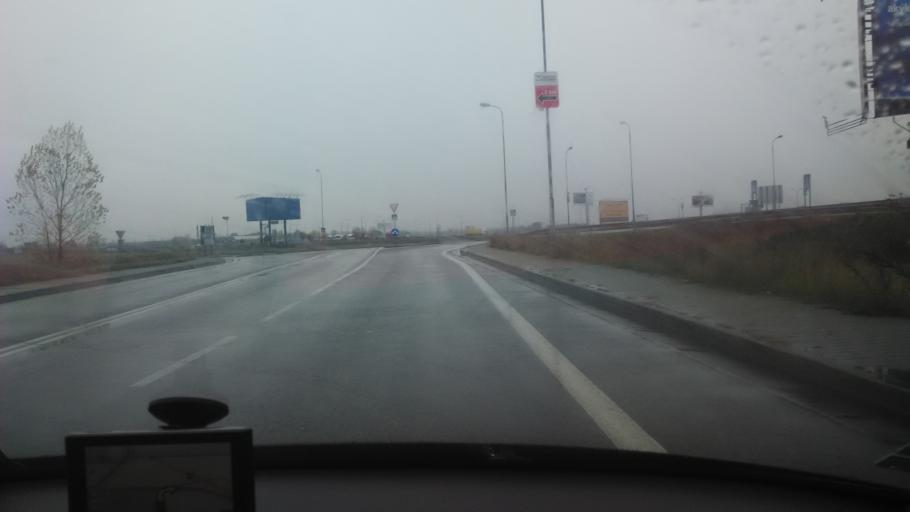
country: SK
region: Bratislavsky
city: Svaty Jur
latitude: 48.1874
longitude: 17.1993
